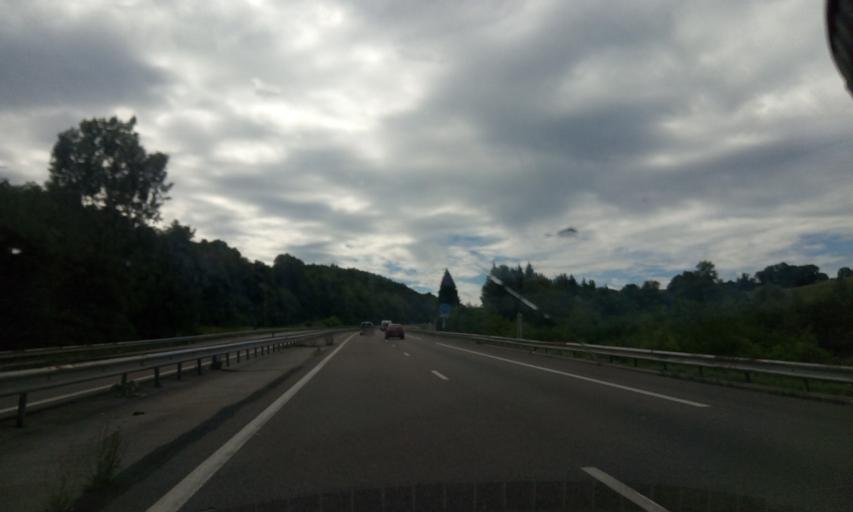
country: FR
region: Rhone-Alpes
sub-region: Departement de l'Isere
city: Chabons
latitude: 45.4706
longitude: 5.4004
